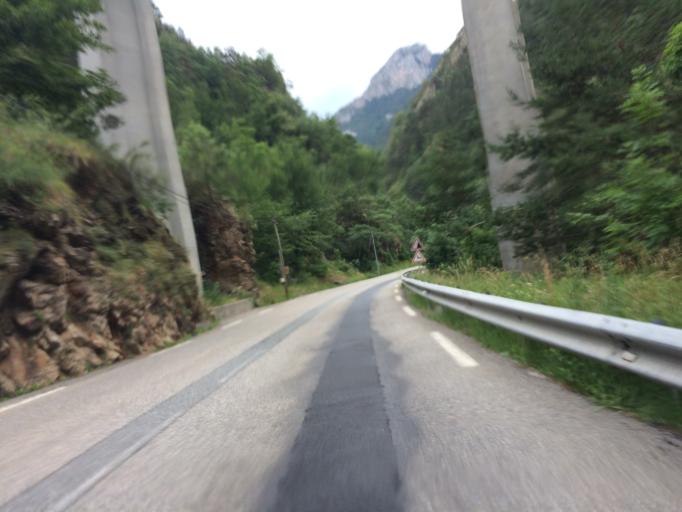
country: FR
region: Provence-Alpes-Cote d'Azur
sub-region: Departement des Alpes-Maritimes
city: Tende
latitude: 44.1096
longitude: 7.5693
